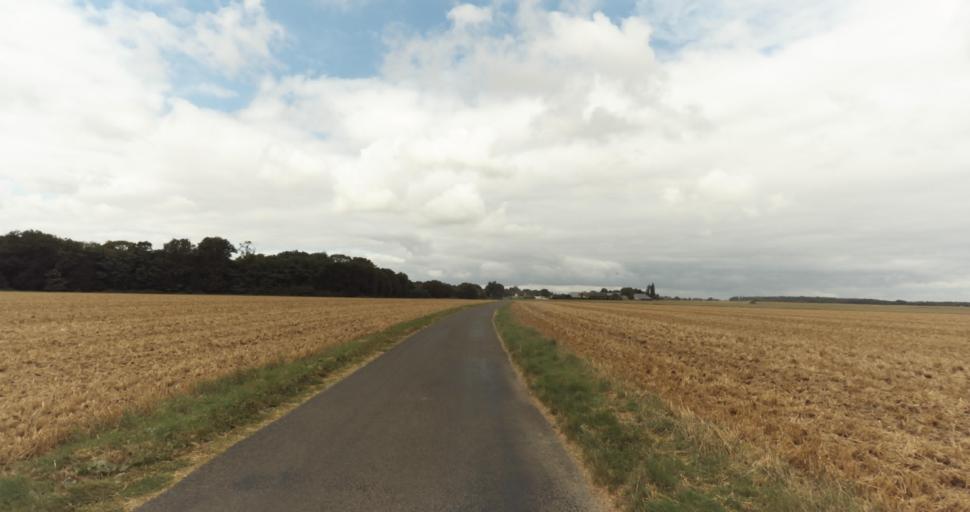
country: FR
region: Haute-Normandie
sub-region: Departement de l'Eure
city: Menilles
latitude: 49.0193
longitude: 1.2815
